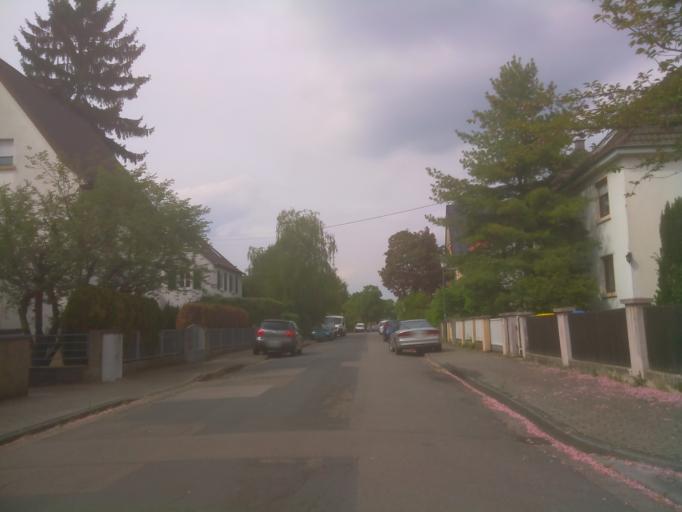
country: DE
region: Baden-Wuerttemberg
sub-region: Karlsruhe Region
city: Heidelberg
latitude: 49.3858
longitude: 8.6889
